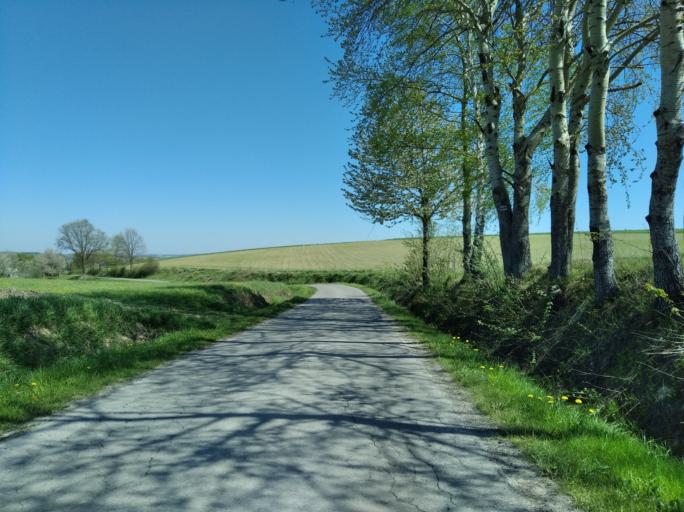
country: PL
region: Subcarpathian Voivodeship
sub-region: Powiat ropczycko-sedziszowski
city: Wielopole Skrzynskie
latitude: 49.9091
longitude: 21.5543
